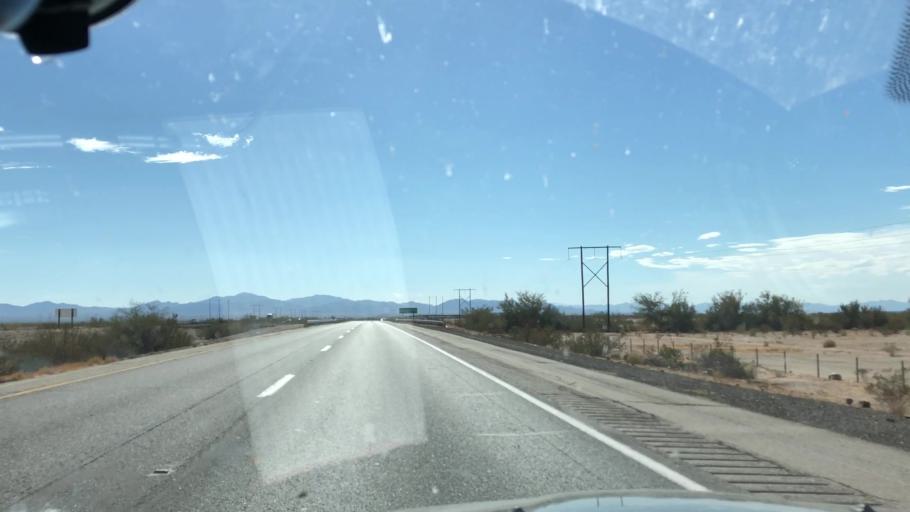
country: US
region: California
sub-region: Riverside County
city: Mesa Verde
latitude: 33.6063
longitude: -114.9719
